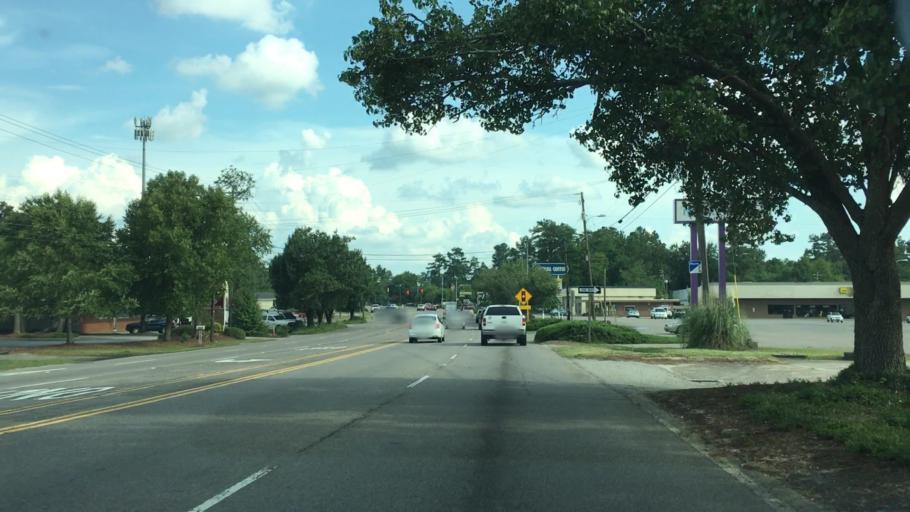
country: US
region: South Carolina
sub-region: Aiken County
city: Aiken
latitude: 33.5329
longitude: -81.7245
